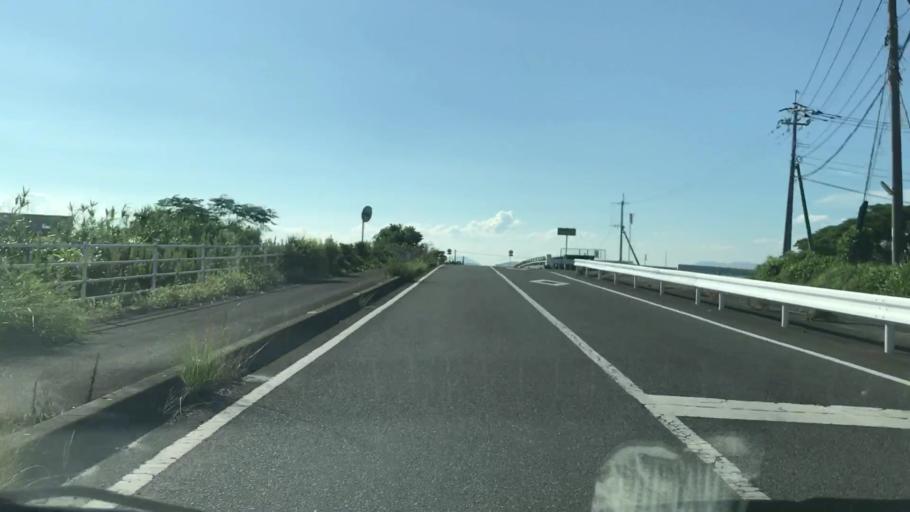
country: JP
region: Saga Prefecture
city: Okawa
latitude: 33.1859
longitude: 130.2919
